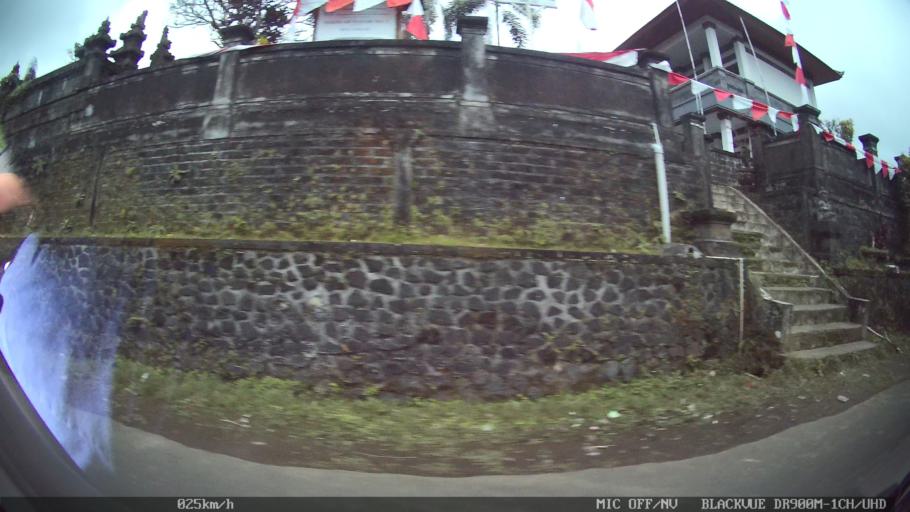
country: ID
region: Bali
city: Peneng
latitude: -8.3529
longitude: 115.2059
